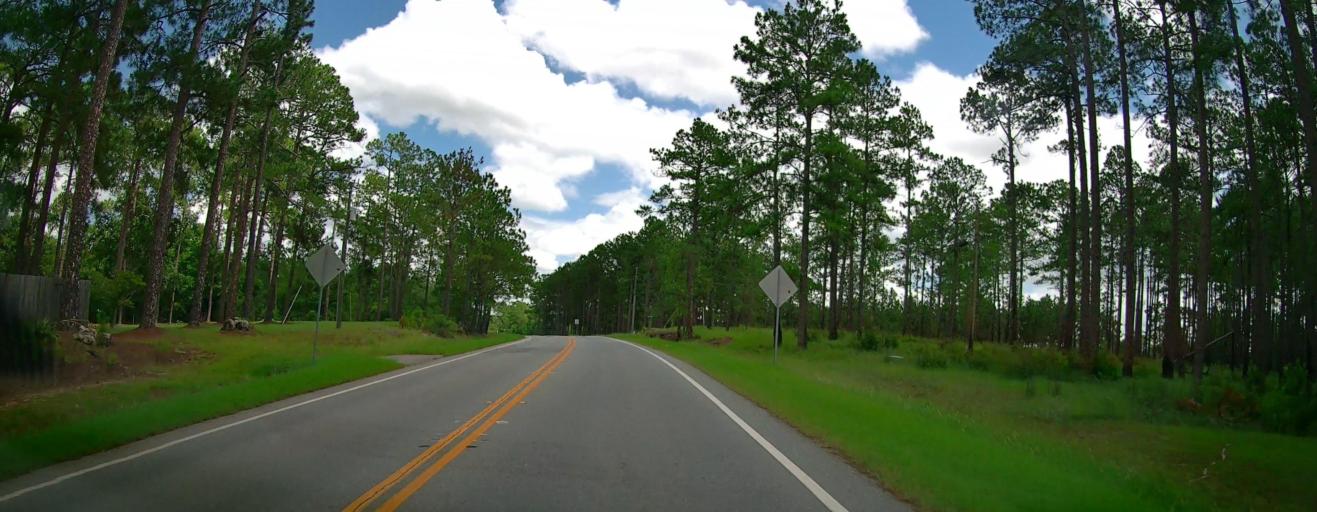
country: US
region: Georgia
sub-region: Turner County
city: Ashburn
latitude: 31.7233
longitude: -83.5821
